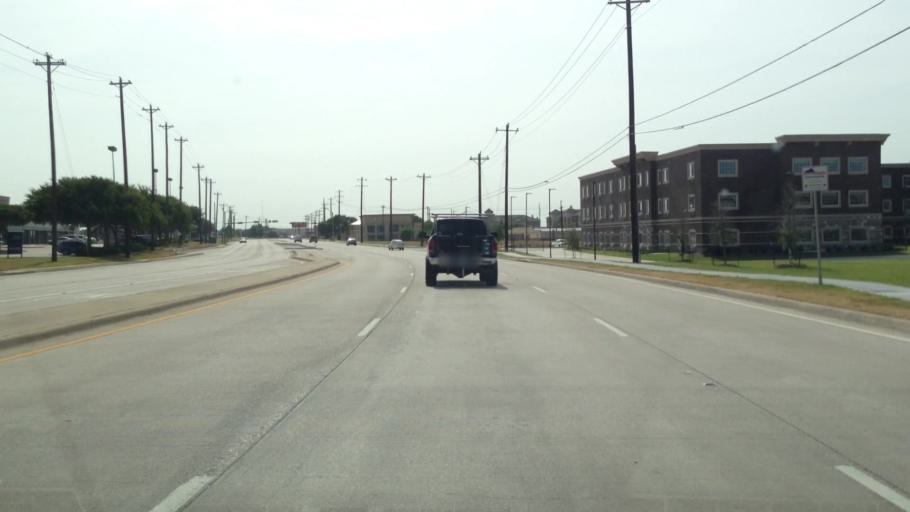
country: US
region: Texas
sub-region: Denton County
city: Lewisville
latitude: 33.0059
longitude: -97.0190
